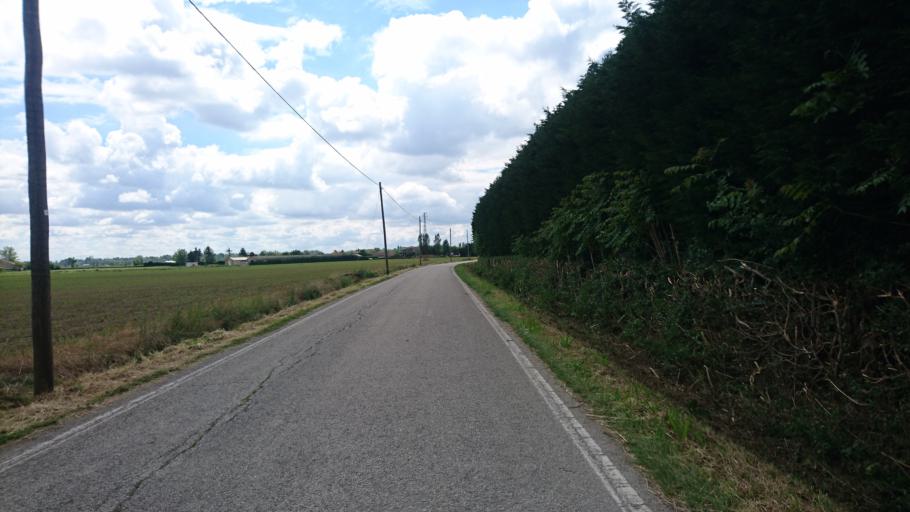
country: IT
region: Veneto
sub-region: Provincia di Padova
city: Villa Estense
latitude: 45.1530
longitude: 11.6494
